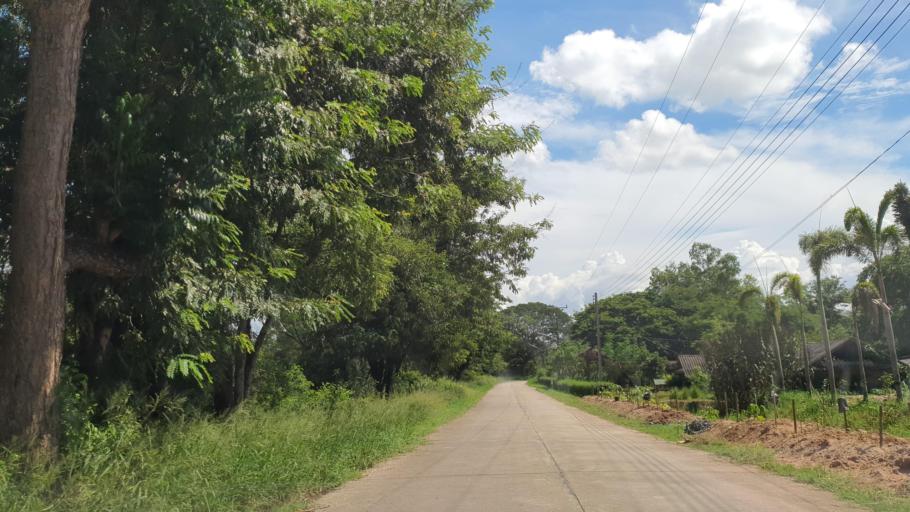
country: TH
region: Chiang Mai
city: San Pa Tong
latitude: 18.5786
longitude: 98.8743
